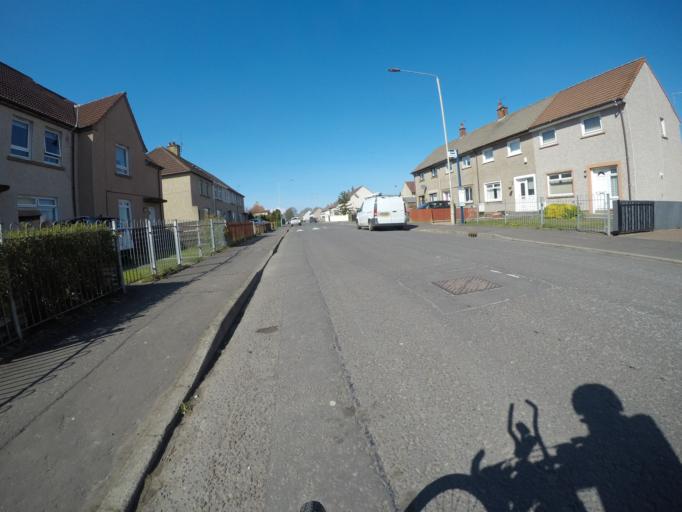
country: GB
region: Scotland
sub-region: North Ayrshire
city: Irvine
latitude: 55.6265
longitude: -4.6671
